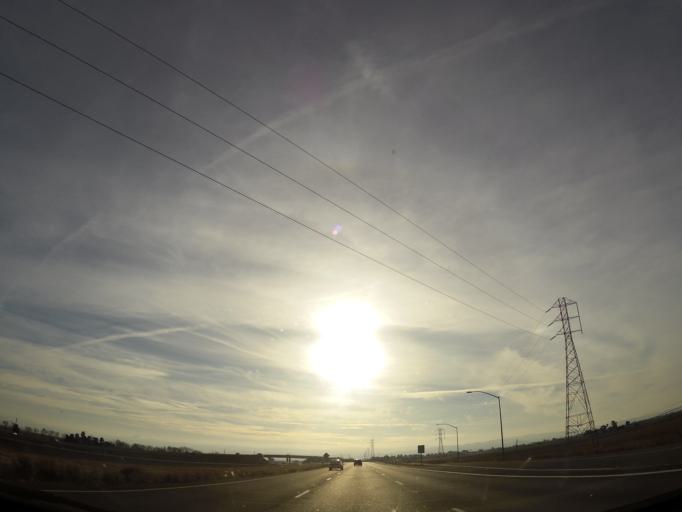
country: US
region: California
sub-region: San Joaquin County
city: Lathrop
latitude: 37.7623
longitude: -121.3388
